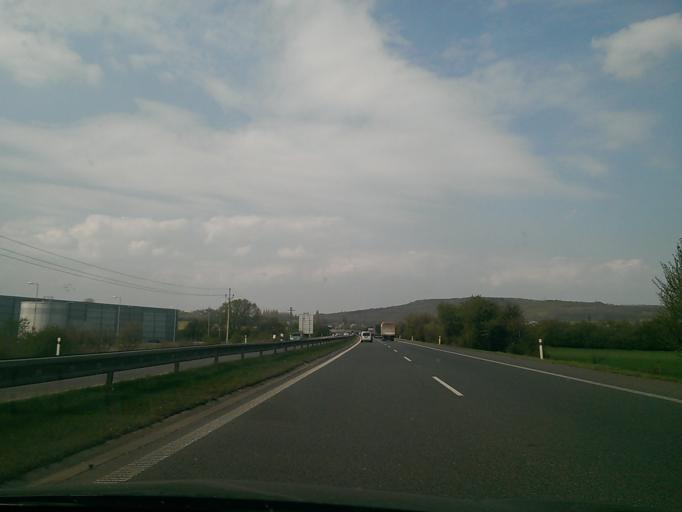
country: CZ
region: Central Bohemia
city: Kosmonosy
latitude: 50.4311
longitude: 14.9437
